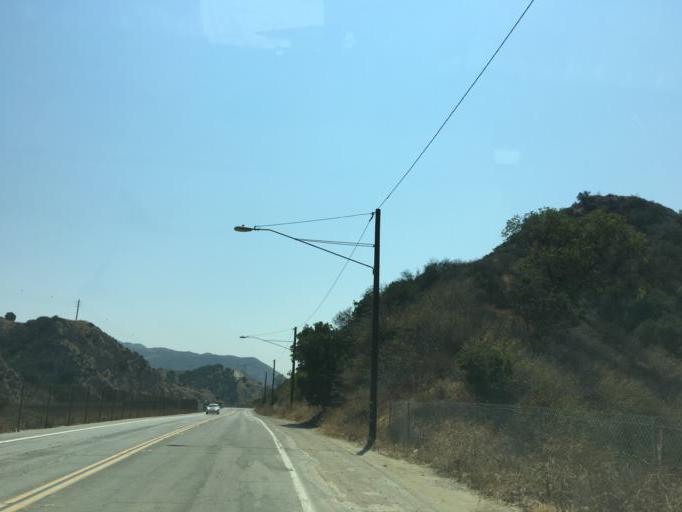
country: US
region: California
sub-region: Los Angeles County
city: Santa Clarita
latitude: 34.3409
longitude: -118.5254
